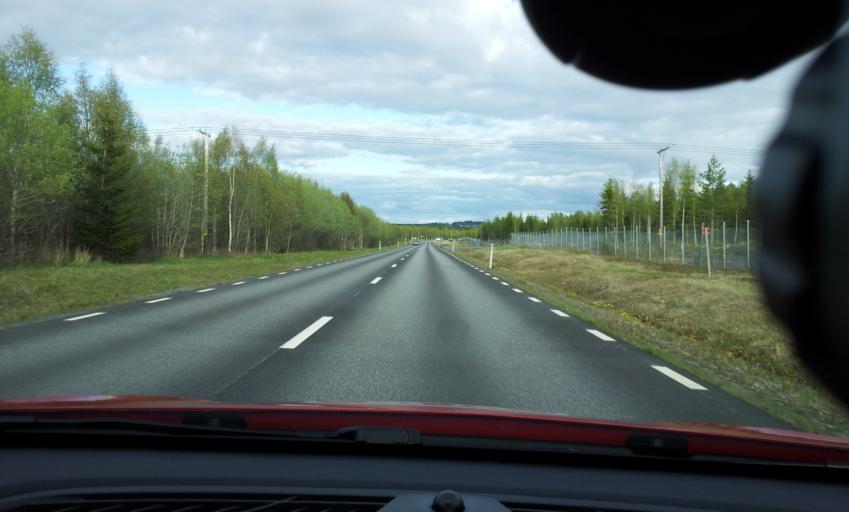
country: SE
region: Jaemtland
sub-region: Krokoms Kommun
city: Krokom
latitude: 63.2028
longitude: 14.4867
